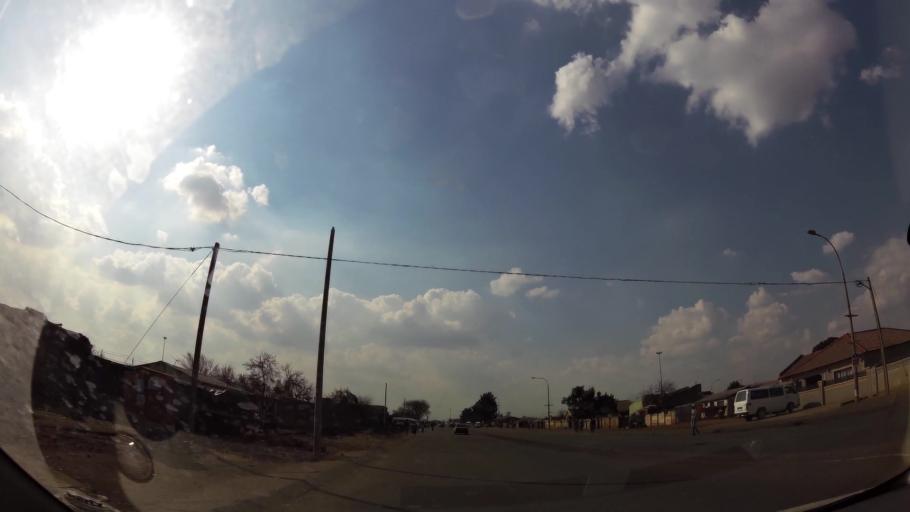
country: ZA
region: Gauteng
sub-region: Ekurhuleni Metropolitan Municipality
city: Germiston
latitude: -26.3344
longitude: 28.1421
